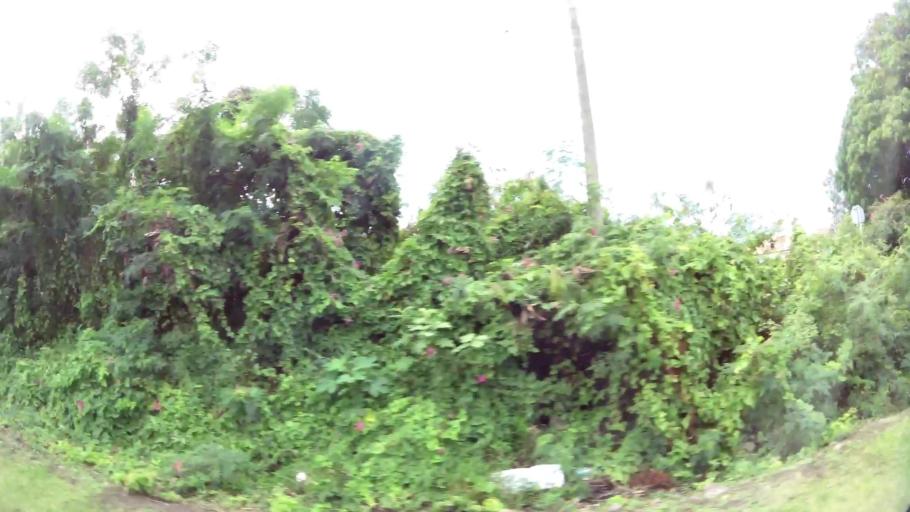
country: KN
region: Saint Paul Charlestown
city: Charlestown
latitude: 17.1274
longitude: -62.6082
